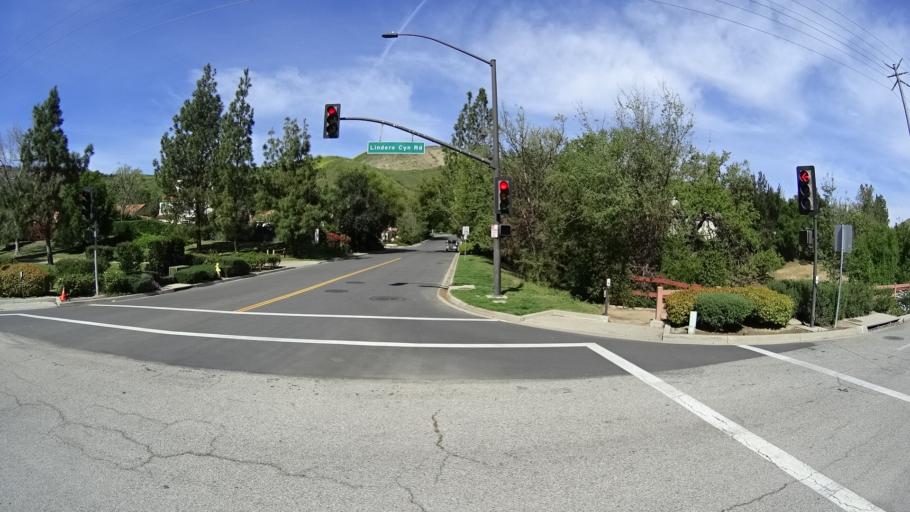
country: US
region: California
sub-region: Ventura County
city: Oak Park
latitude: 34.1757
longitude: -118.7876
